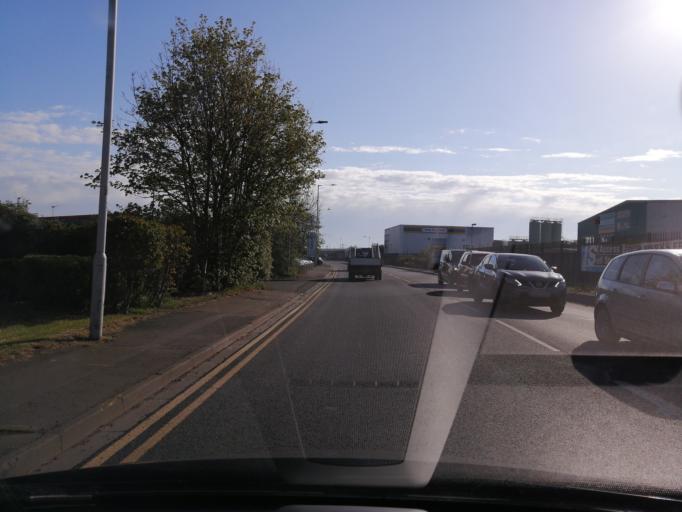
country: GB
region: England
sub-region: Peterborough
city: Peterborough
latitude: 52.5711
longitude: -0.2144
